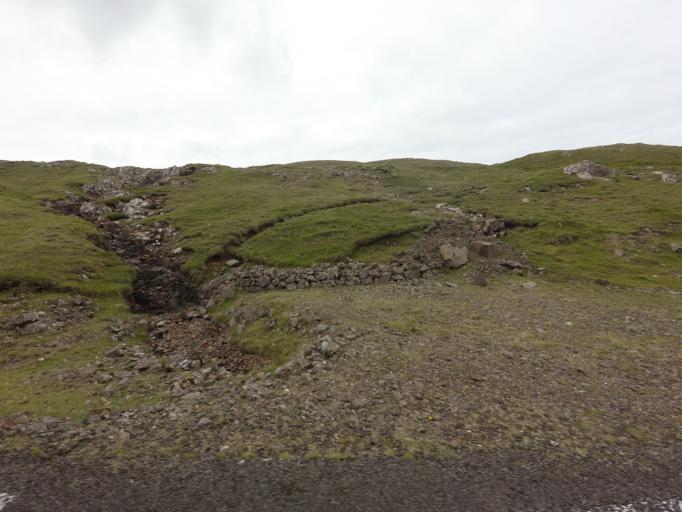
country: FO
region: Suduroy
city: Vagur
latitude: 61.4412
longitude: -6.7378
